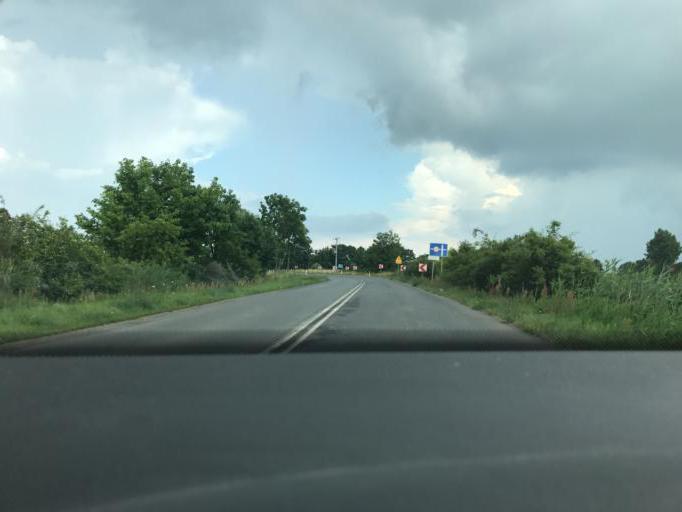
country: PL
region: Pomeranian Voivodeship
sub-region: Powiat gdanski
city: Cedry Wielkie
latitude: 54.3352
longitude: 18.8211
